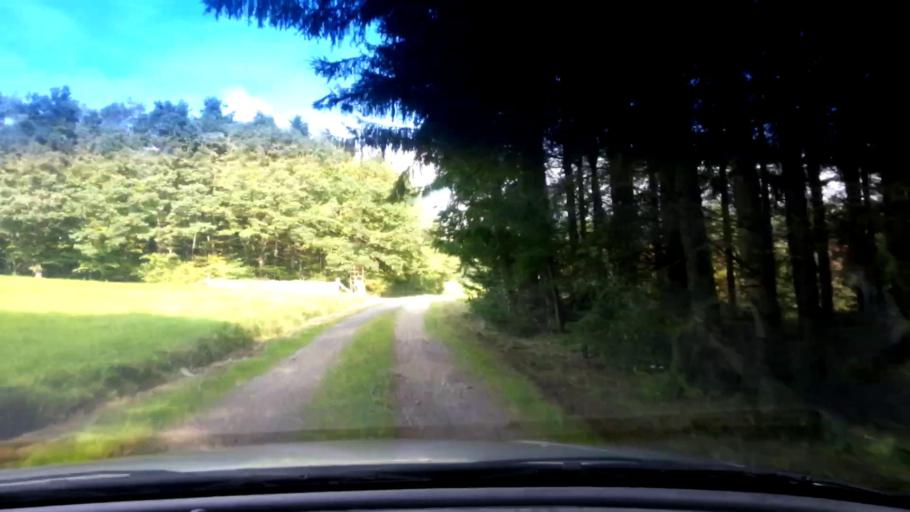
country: DE
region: Bavaria
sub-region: Upper Franconia
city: Gundelsheim
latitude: 49.9727
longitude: 10.9412
